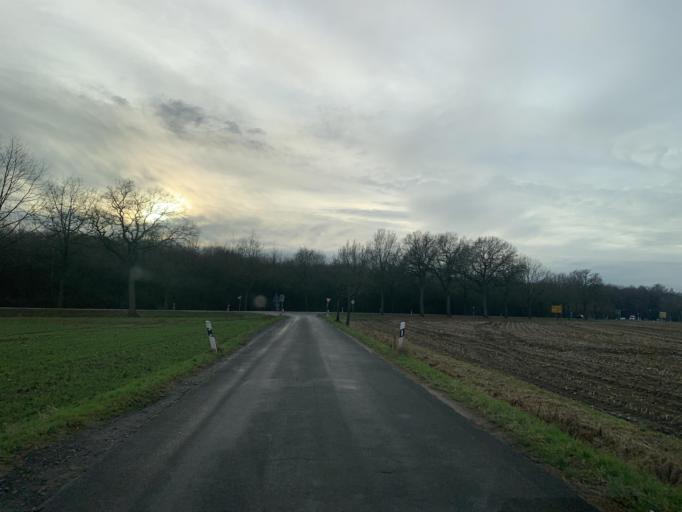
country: DE
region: North Rhine-Westphalia
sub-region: Regierungsbezirk Munster
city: Dulmen
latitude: 51.8371
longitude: 7.3233
